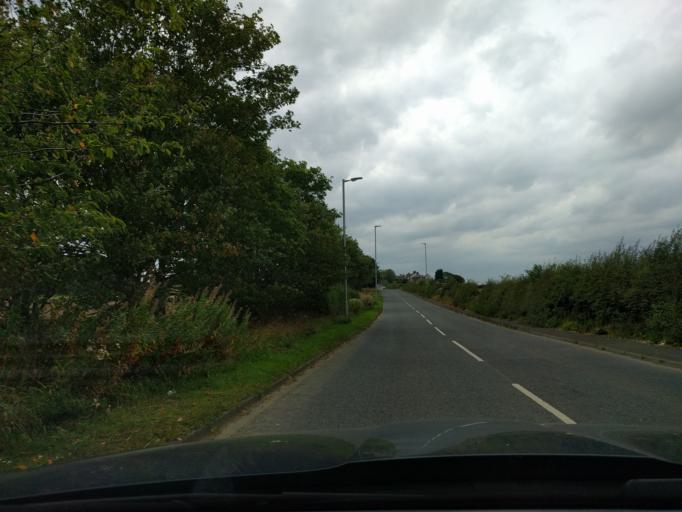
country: GB
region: England
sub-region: Northumberland
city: Choppington
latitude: 55.1331
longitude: -1.6261
